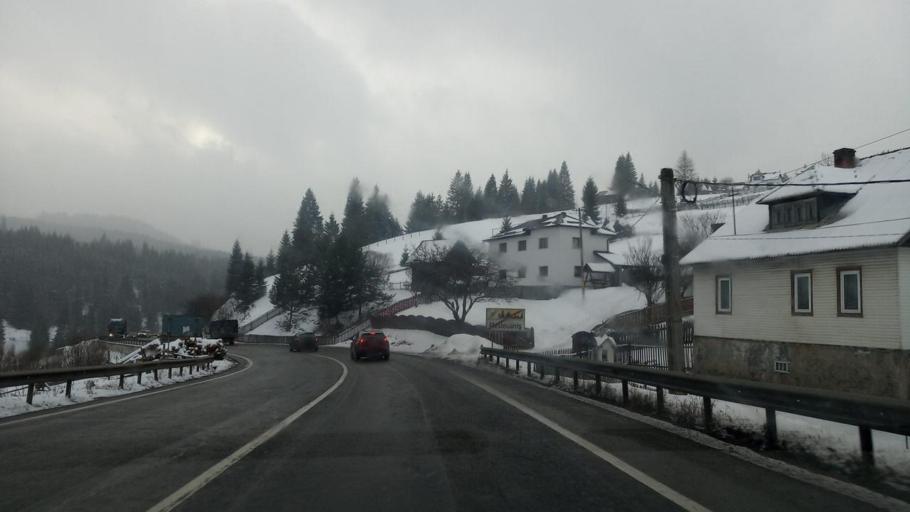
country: RO
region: Suceava
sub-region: Comuna Iacobeni
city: Iacobeni
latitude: 47.4518
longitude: 25.3322
